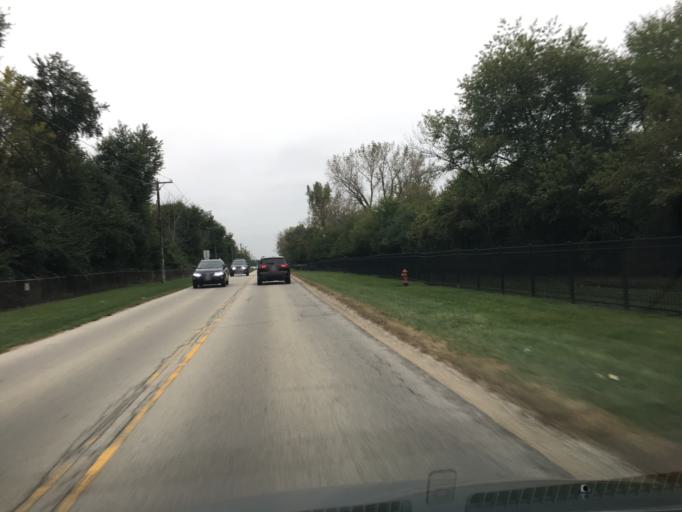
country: US
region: Illinois
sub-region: Will County
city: Plainfield
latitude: 41.6437
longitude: -88.1646
